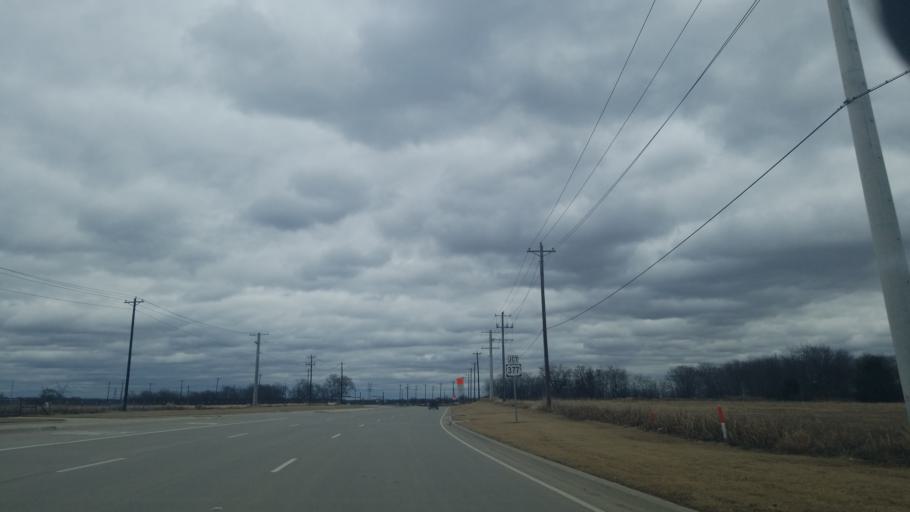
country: US
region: Texas
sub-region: Denton County
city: Roanoke
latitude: 33.0570
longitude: -97.2068
